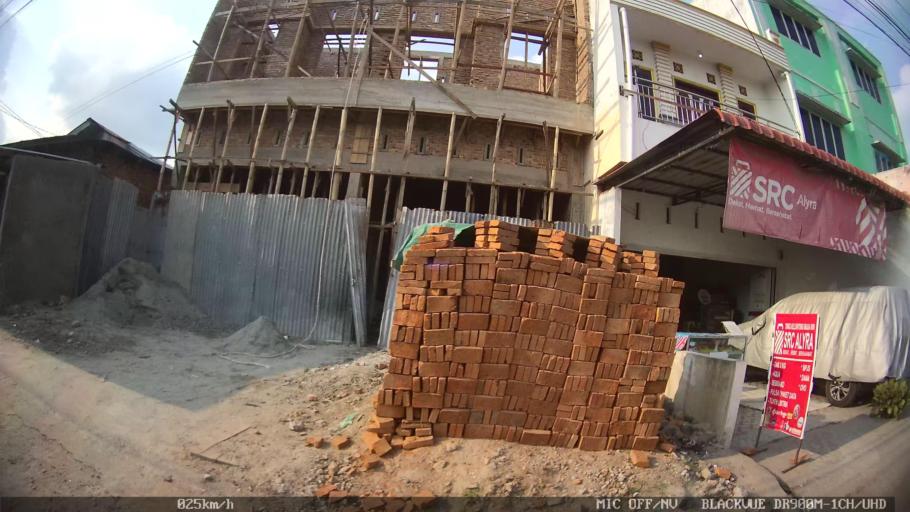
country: ID
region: North Sumatra
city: Medan
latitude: 3.5852
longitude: 98.7511
